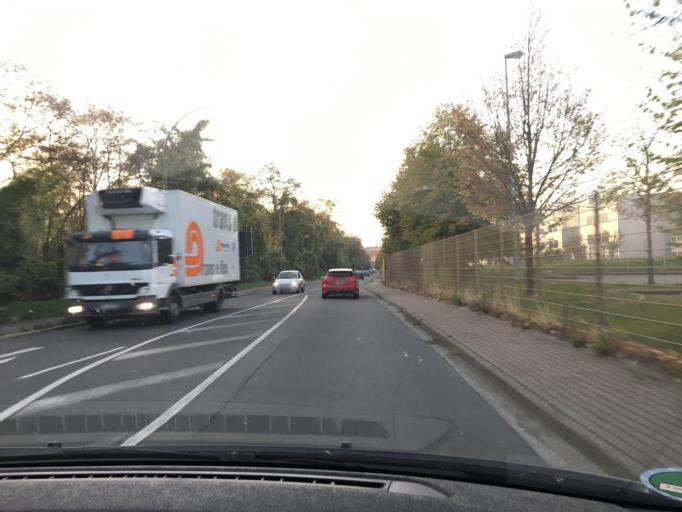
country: DE
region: North Rhine-Westphalia
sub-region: Regierungsbezirk Koln
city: Hurth
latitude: 50.8584
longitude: 6.8349
